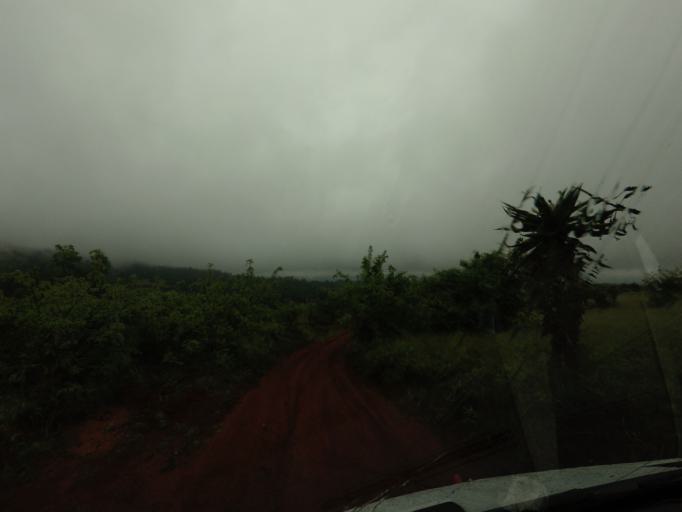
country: SZ
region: Hhohho
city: Lobamba
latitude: -26.4656
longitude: 31.1777
